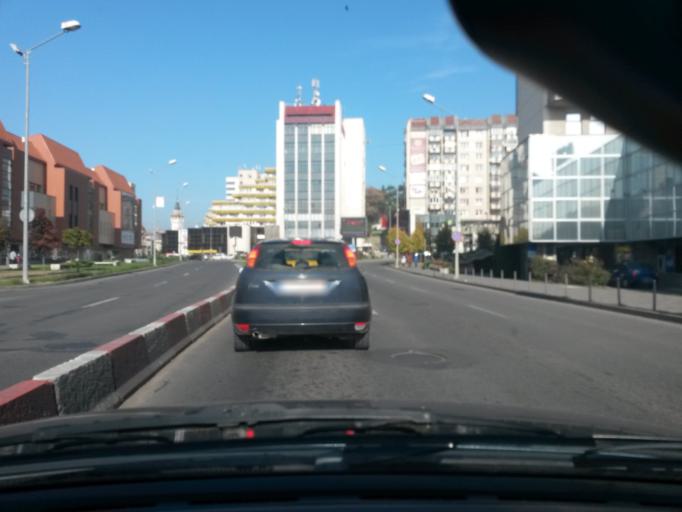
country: RO
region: Mures
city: Targu-Mures
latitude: 46.5390
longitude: 24.5583
